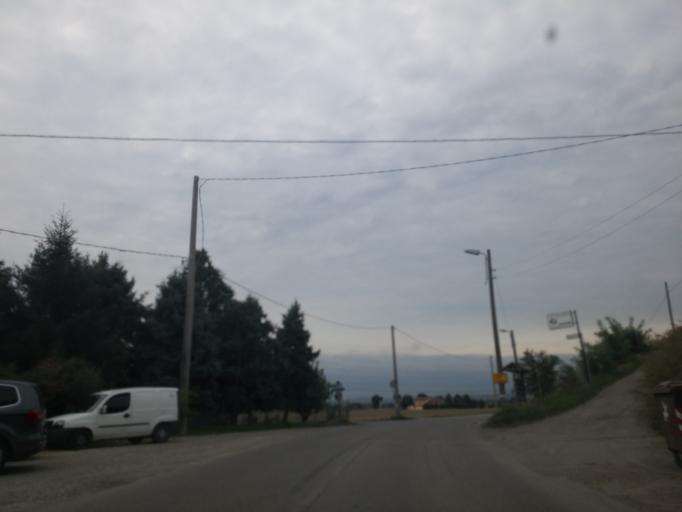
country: IT
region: Emilia-Romagna
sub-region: Provincia di Bologna
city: Longara
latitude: 44.5955
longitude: 11.3230
